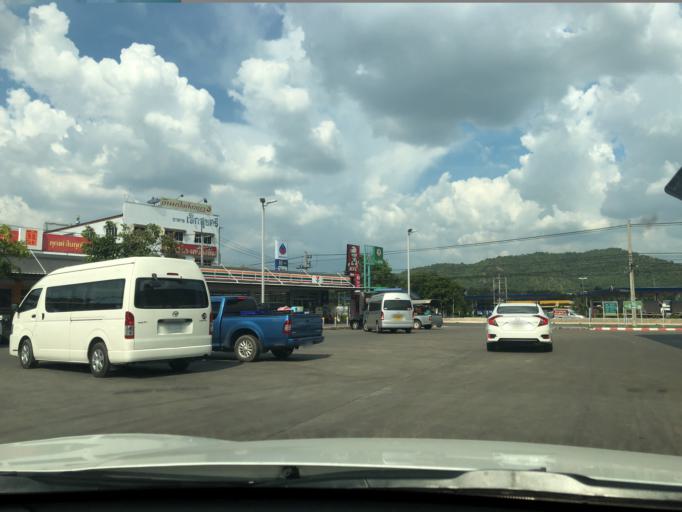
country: TH
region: Nakhon Sawan
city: Krok Phra
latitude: 15.5774
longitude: 100.1240
